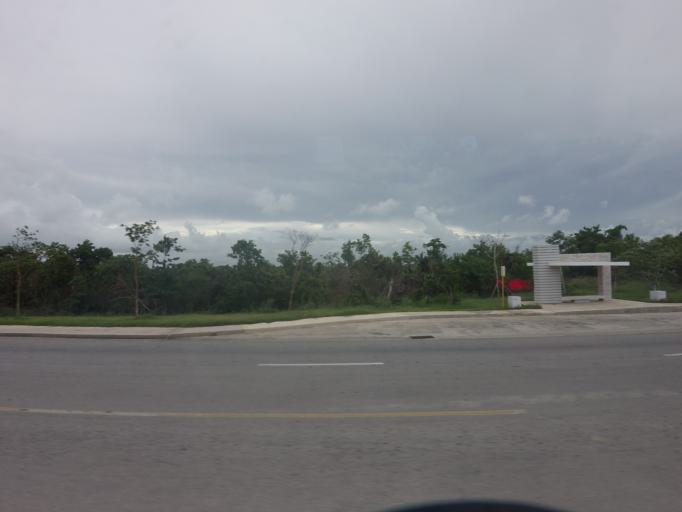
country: CU
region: Matanzas
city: Varadero
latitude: 23.1936
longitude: -81.1533
